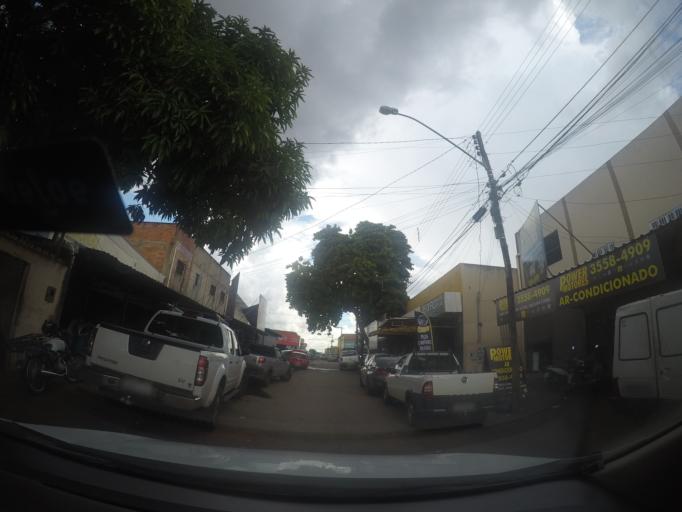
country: BR
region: Goias
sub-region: Goiania
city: Goiania
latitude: -16.6949
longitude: -49.3168
